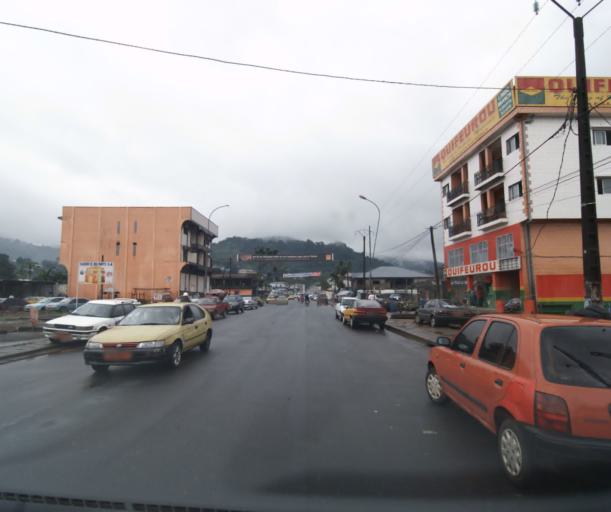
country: CM
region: South-West Province
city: Limbe
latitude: 4.0155
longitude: 9.2100
